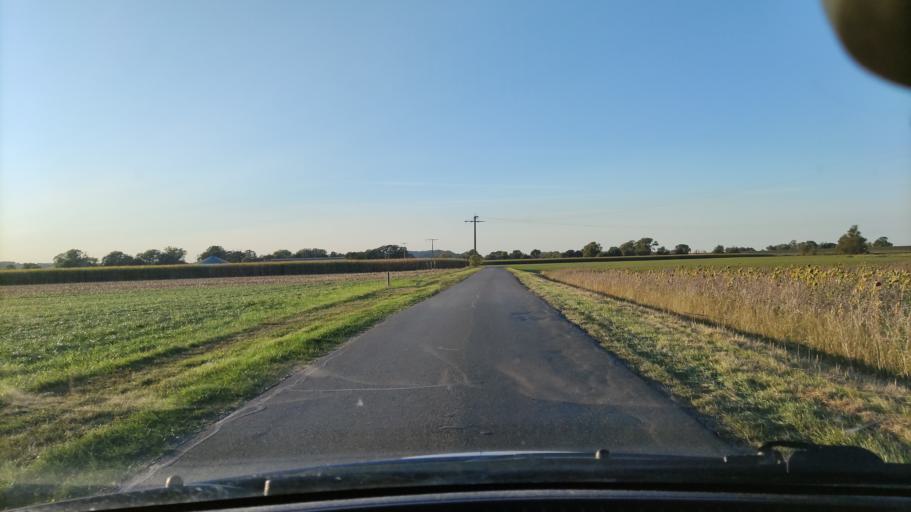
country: DE
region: Lower Saxony
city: Dannenberg
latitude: 53.1307
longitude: 11.0761
